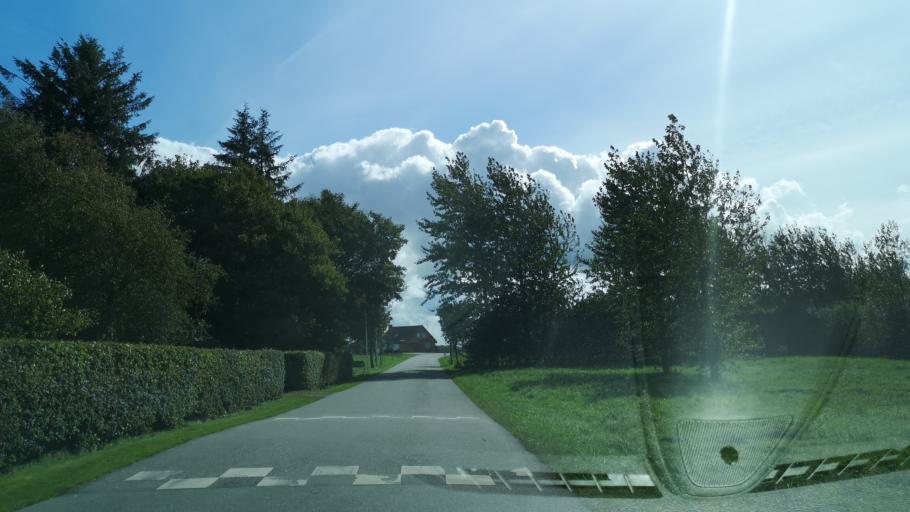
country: DK
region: Central Jutland
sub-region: Ringkobing-Skjern Kommune
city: Skjern
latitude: 55.9827
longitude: 8.5481
